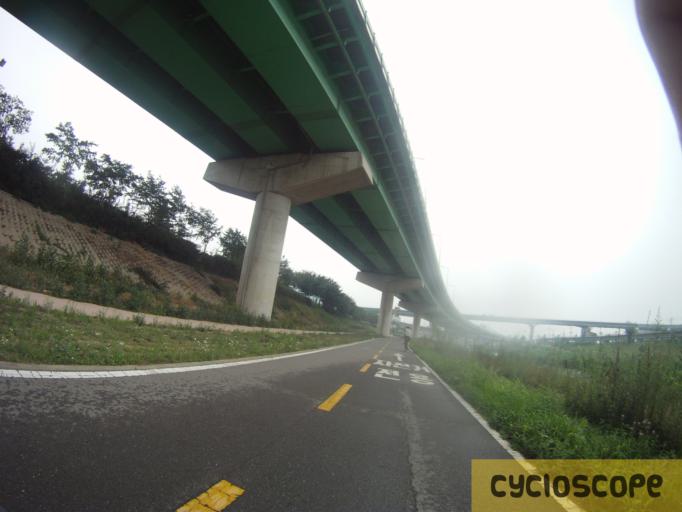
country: KR
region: Gyeonggi-do
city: Kwangmyong
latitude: 37.4433
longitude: 126.8990
